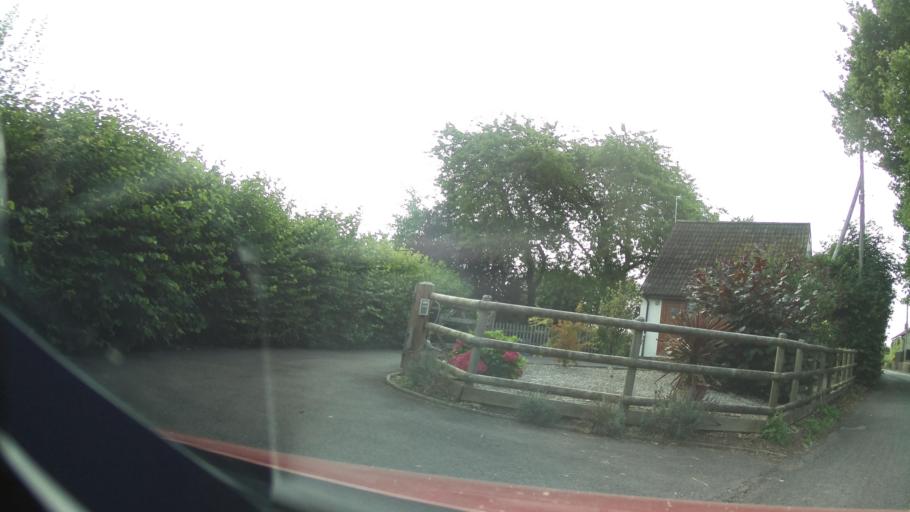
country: GB
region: England
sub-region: Bath and North East Somerset
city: Compton Martin
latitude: 51.3141
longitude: -2.6367
